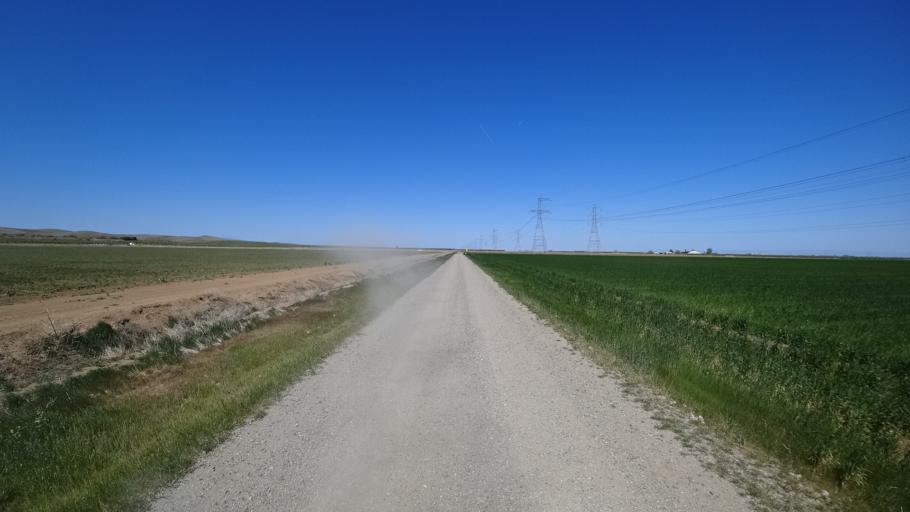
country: US
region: California
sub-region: Glenn County
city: Willows
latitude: 39.4765
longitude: -122.2866
